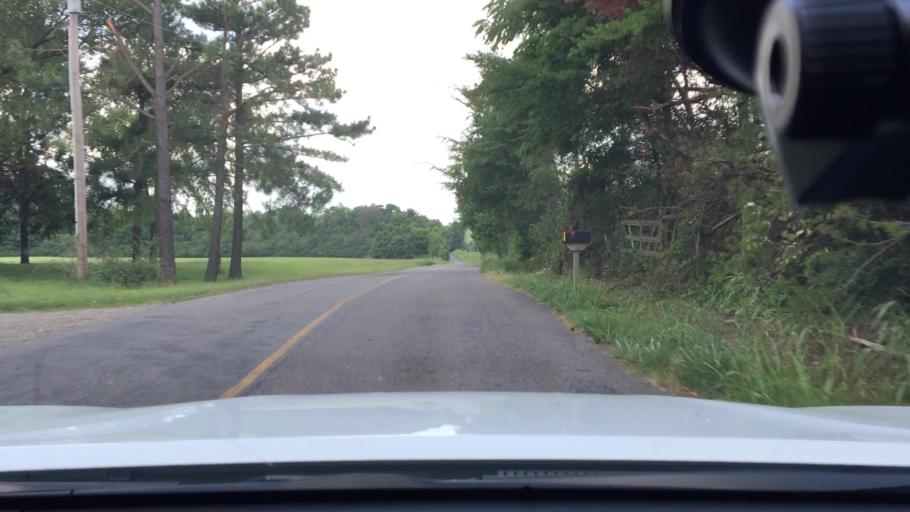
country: US
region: Arkansas
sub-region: Logan County
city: Paris
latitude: 35.2692
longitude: -93.6751
